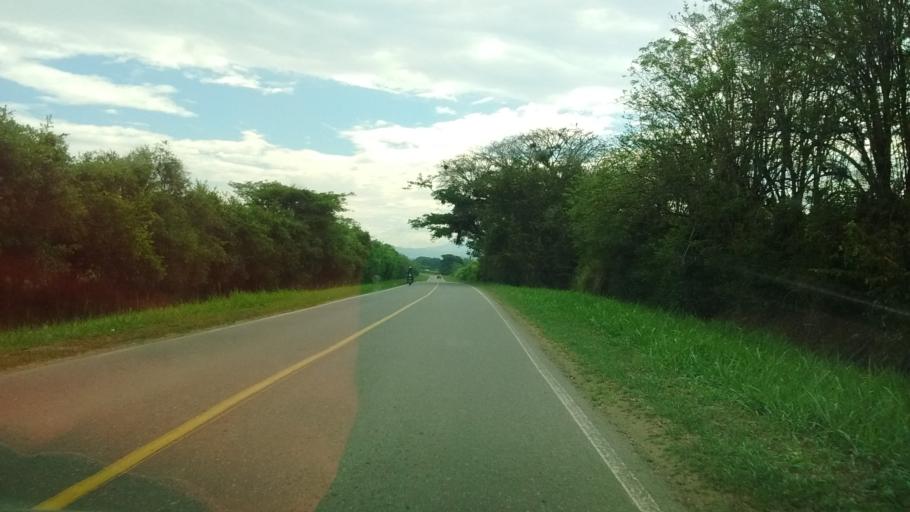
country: CO
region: Cauca
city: Santander de Quilichao
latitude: 3.0412
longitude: -76.4594
